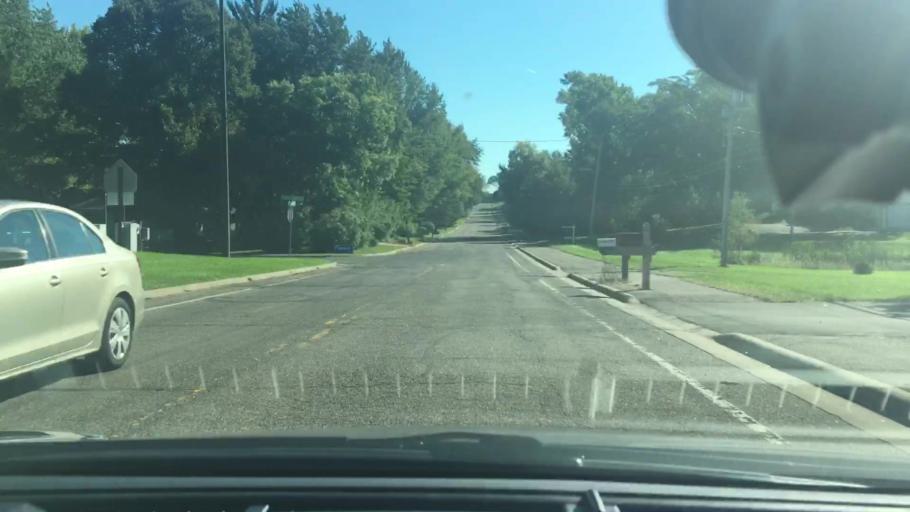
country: US
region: Minnesota
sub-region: Hennepin County
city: Minnetonka Mills
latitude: 44.9788
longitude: -93.4298
